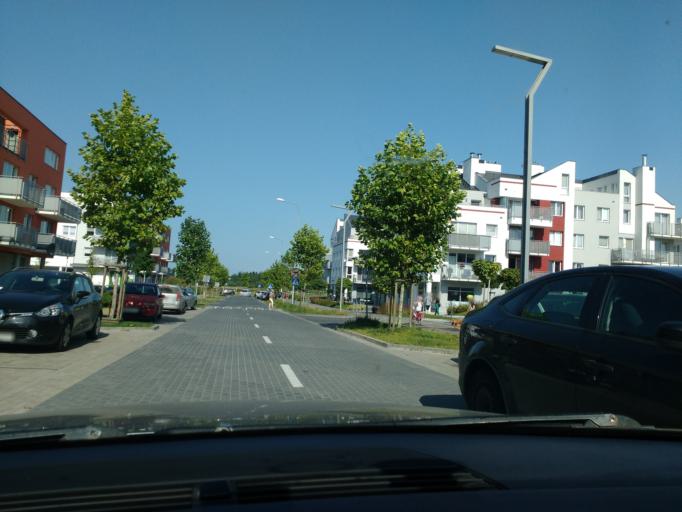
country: PL
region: Pomeranian Voivodeship
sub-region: Powiat kartuski
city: Chwaszczyno
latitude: 54.4859
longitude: 18.4278
